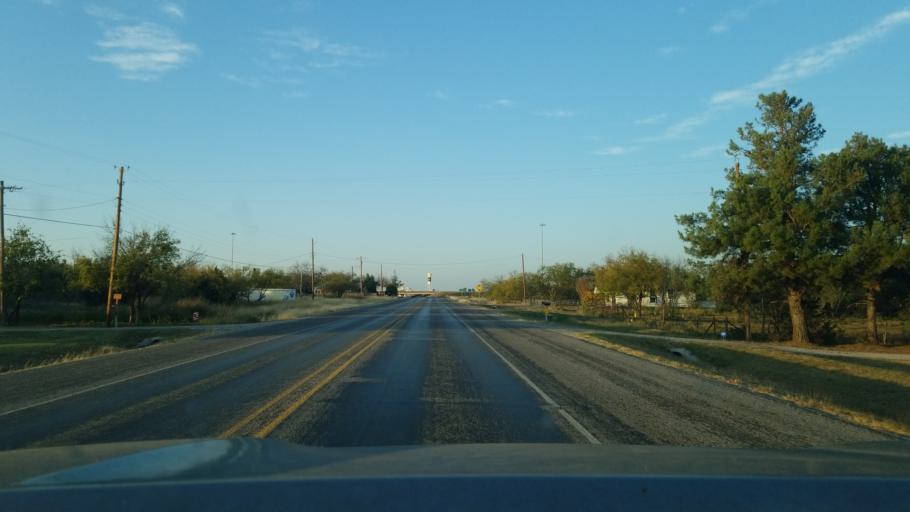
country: US
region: Texas
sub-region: Eastland County
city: Cisco
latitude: 32.3700
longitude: -98.9702
